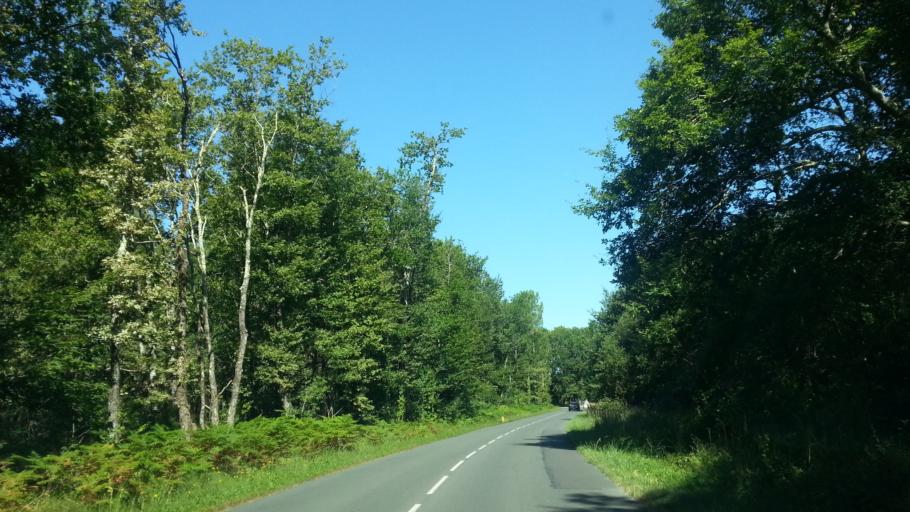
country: FR
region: Aquitaine
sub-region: Departement de la Gironde
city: Saint-Selve
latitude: 44.6716
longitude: -0.4882
